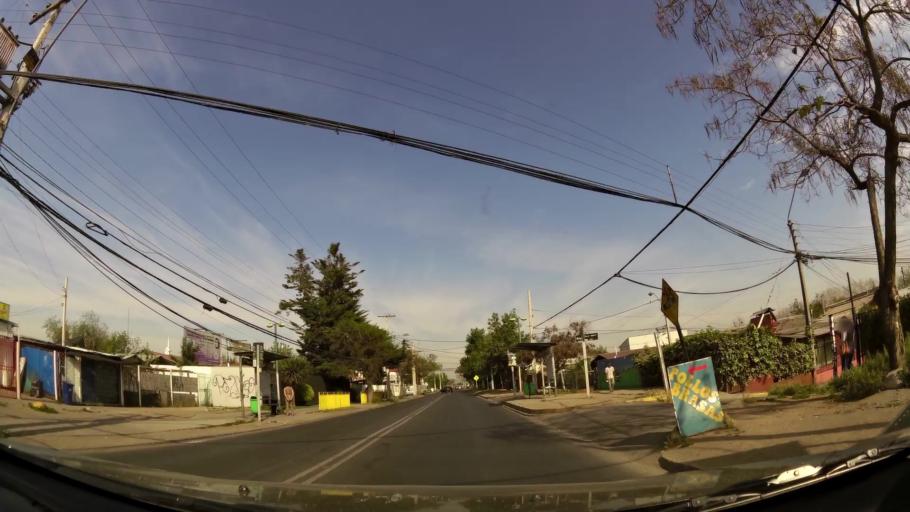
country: CL
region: Santiago Metropolitan
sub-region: Provincia de Cordillera
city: Puente Alto
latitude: -33.5601
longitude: -70.5638
